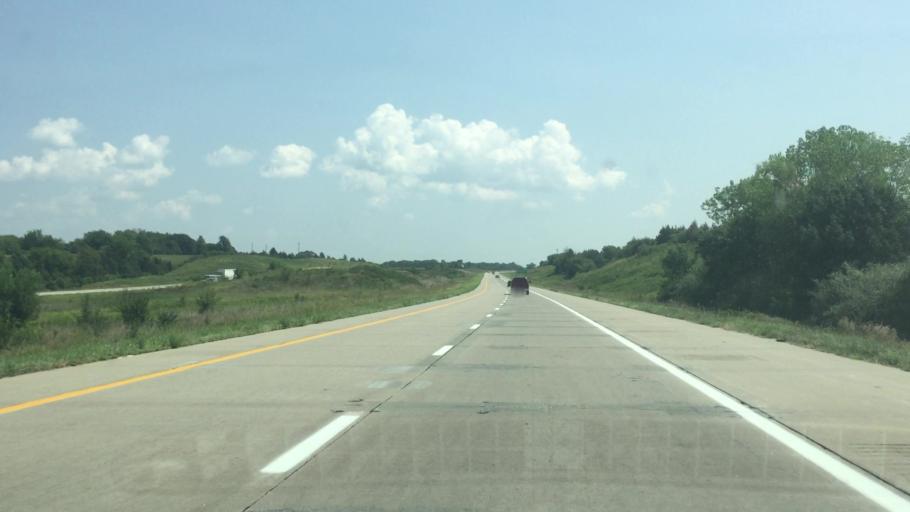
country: US
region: Kansas
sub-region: Franklin County
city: Ottawa
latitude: 38.5637
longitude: -95.3075
